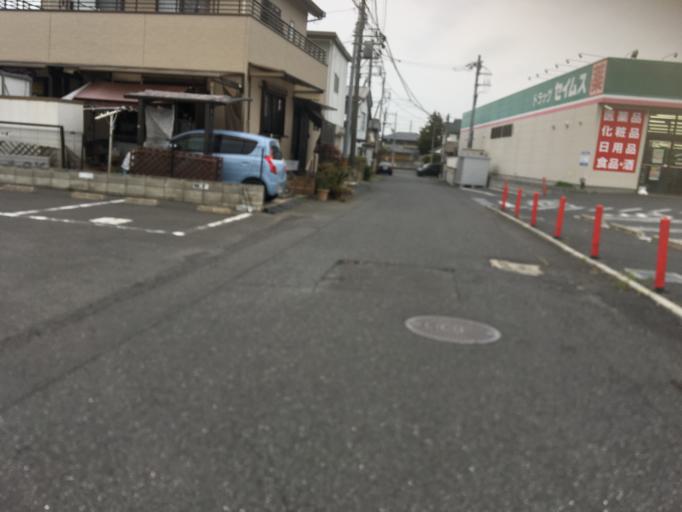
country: JP
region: Saitama
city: Kazo
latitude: 36.1251
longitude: 139.6050
